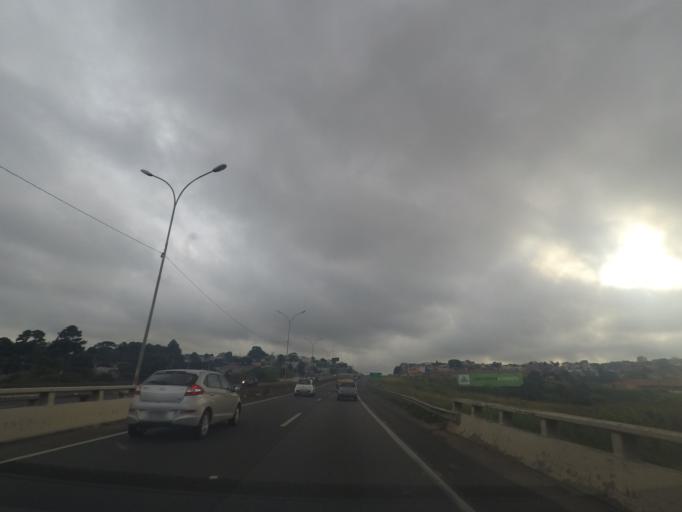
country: BR
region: Parana
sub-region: Pinhais
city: Pinhais
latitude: -25.3871
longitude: -49.1770
